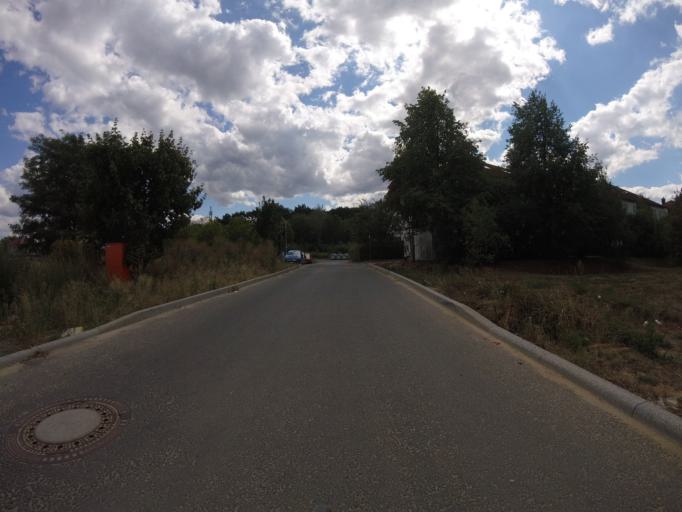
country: DE
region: Brandenburg
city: Werder
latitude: 52.4133
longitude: 12.9796
